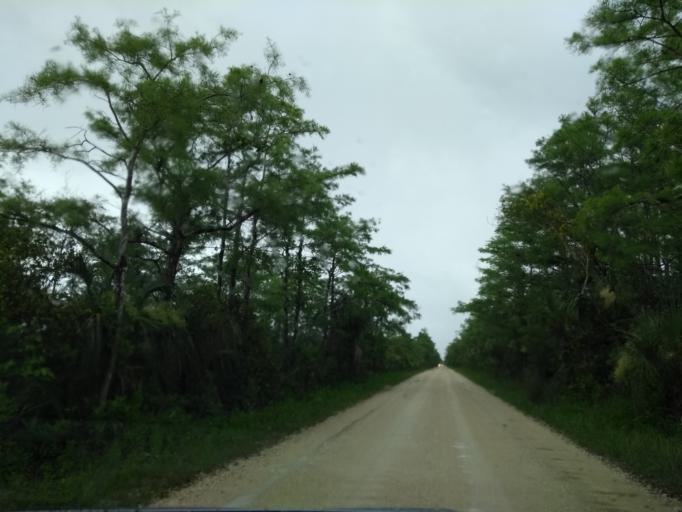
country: US
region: Florida
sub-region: Miami-Dade County
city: The Hammocks
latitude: 25.7602
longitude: -81.0258
